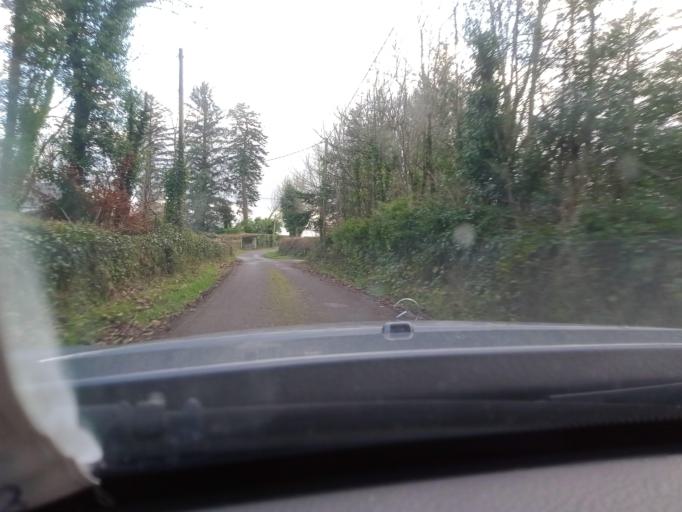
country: IE
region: Leinster
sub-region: Kilkenny
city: Graiguenamanagh
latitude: 52.5099
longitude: -6.9417
